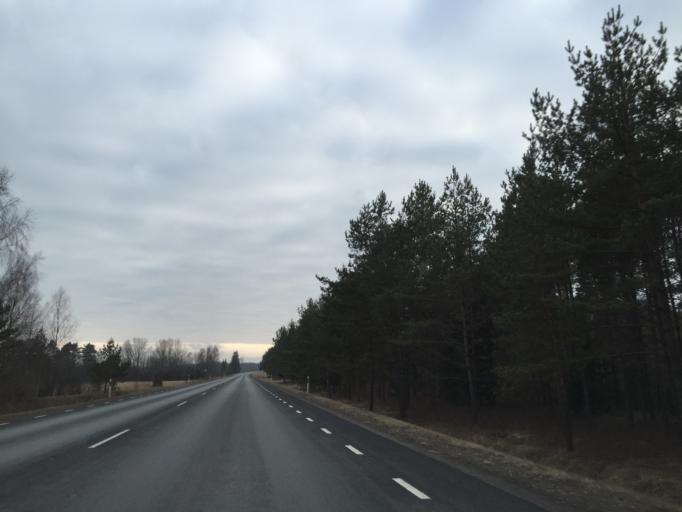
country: EE
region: Saare
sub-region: Orissaare vald
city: Orissaare
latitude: 58.5270
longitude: 22.9134
